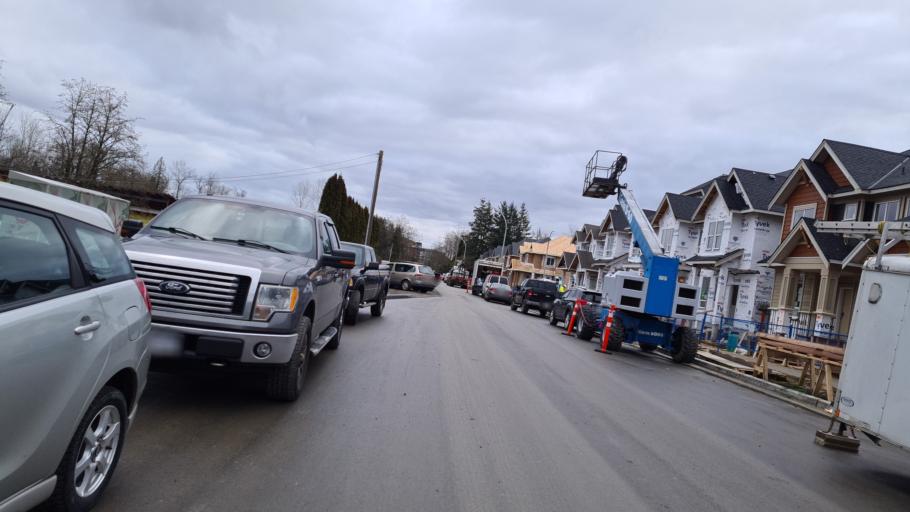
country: CA
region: British Columbia
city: Walnut Grove
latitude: 49.1445
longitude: -122.6561
